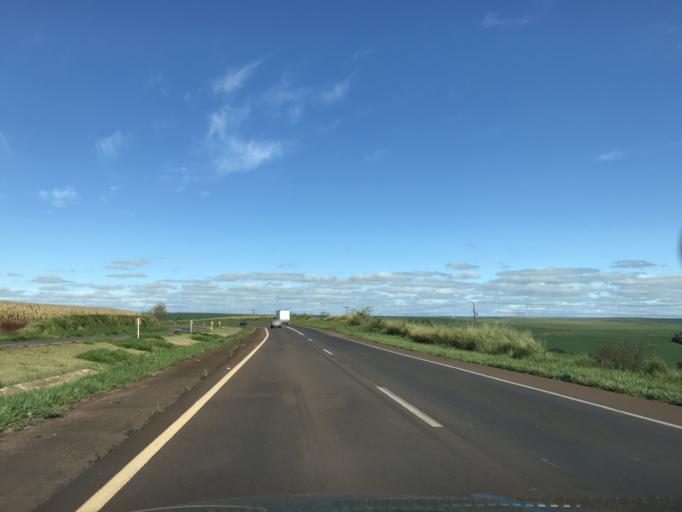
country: BR
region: Parana
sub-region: Cascavel
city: Cascavel
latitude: -24.8500
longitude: -53.6037
